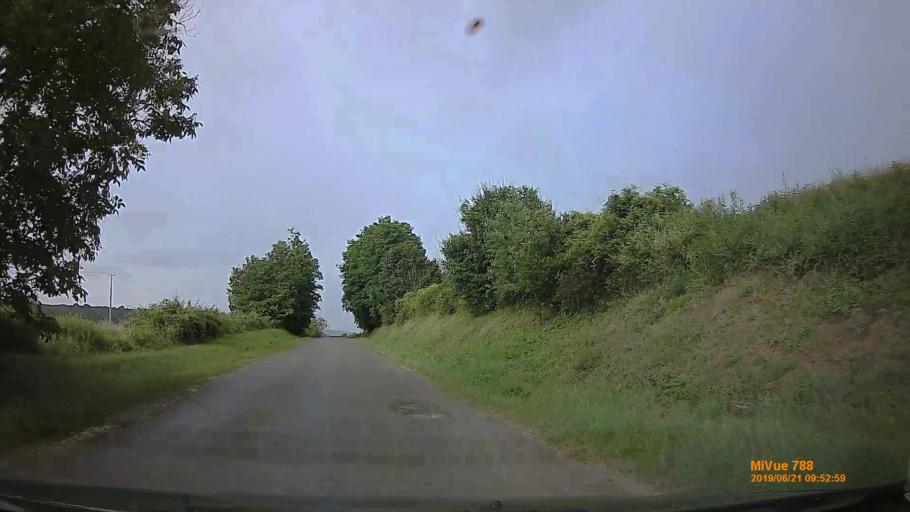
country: HU
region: Baranya
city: Sasd
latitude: 46.2394
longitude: 18.0122
